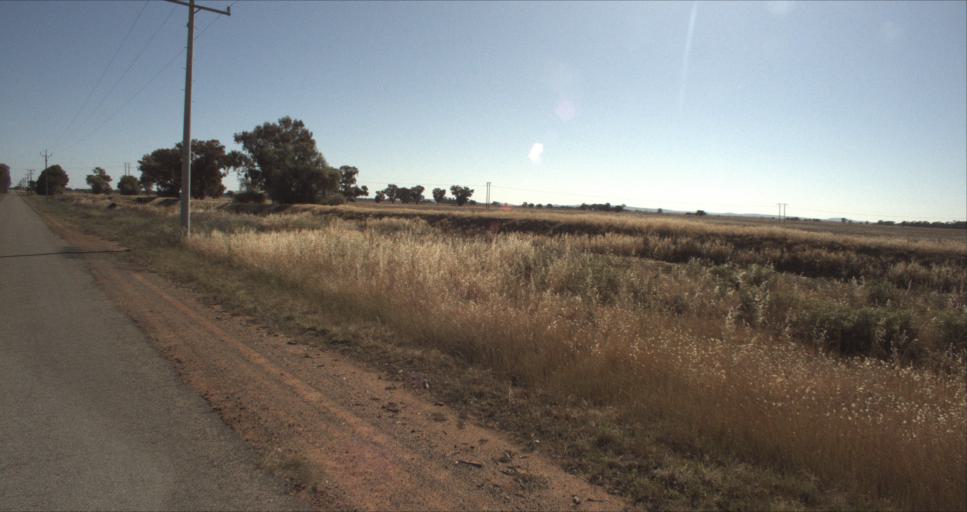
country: AU
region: New South Wales
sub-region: Leeton
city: Leeton
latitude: -34.5780
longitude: 146.3093
